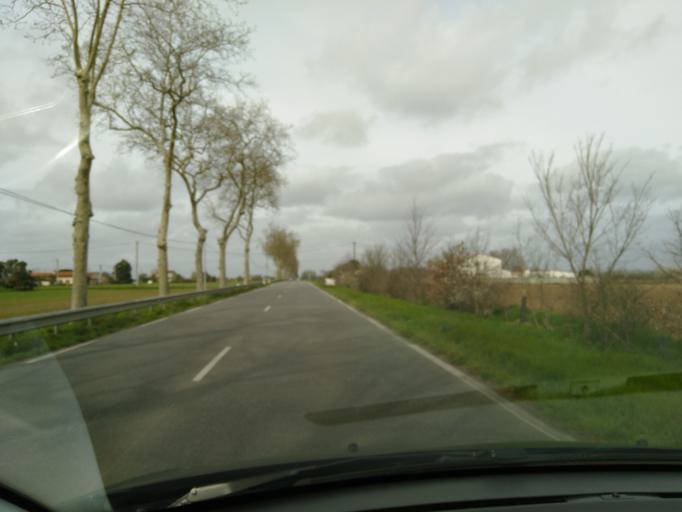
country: FR
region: Midi-Pyrenees
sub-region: Departement de la Haute-Garonne
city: Merville
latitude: 43.7247
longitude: 1.3261
